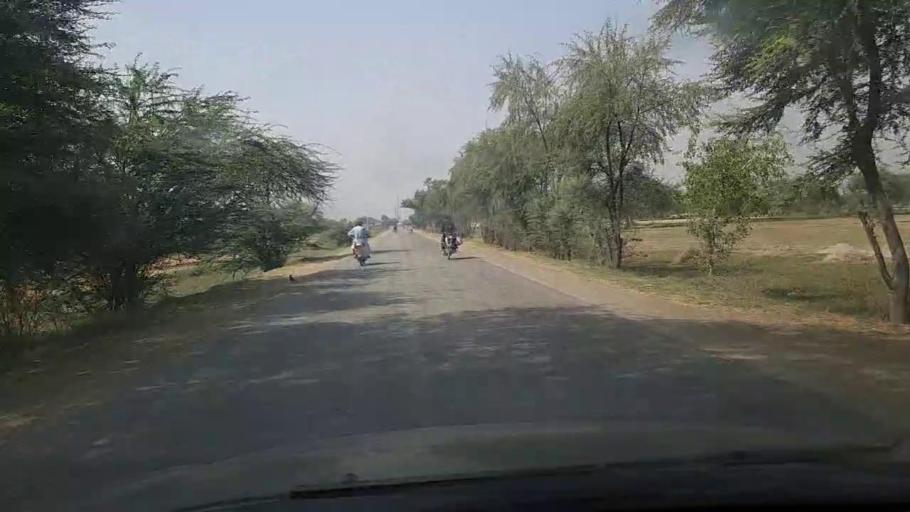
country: PK
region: Sindh
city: Mirpur Mathelo
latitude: 27.9242
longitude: 69.5285
